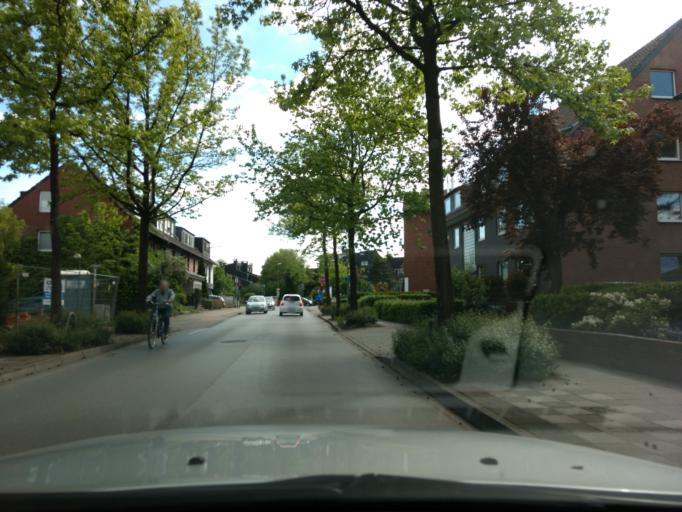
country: DE
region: North Rhine-Westphalia
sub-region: Regierungsbezirk Dusseldorf
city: Meerbusch
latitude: 51.2432
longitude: 6.7020
